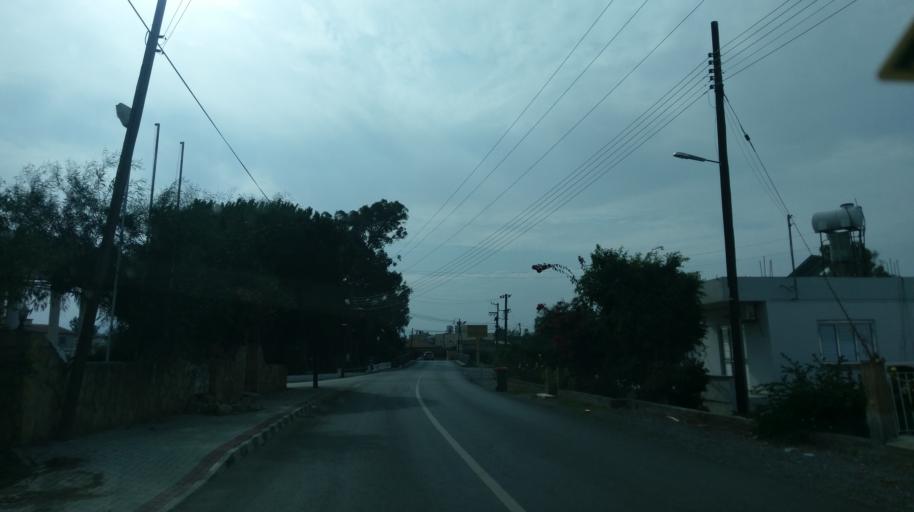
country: CY
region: Lefkosia
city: Morfou
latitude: 35.1690
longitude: 33.0101
